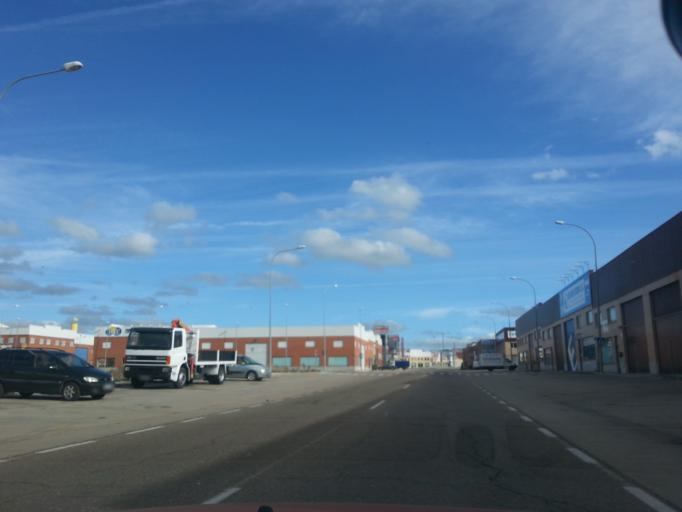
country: ES
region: Castille and Leon
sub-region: Provincia de Salamanca
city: Villares de la Reina
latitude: 40.9953
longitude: -5.6489
